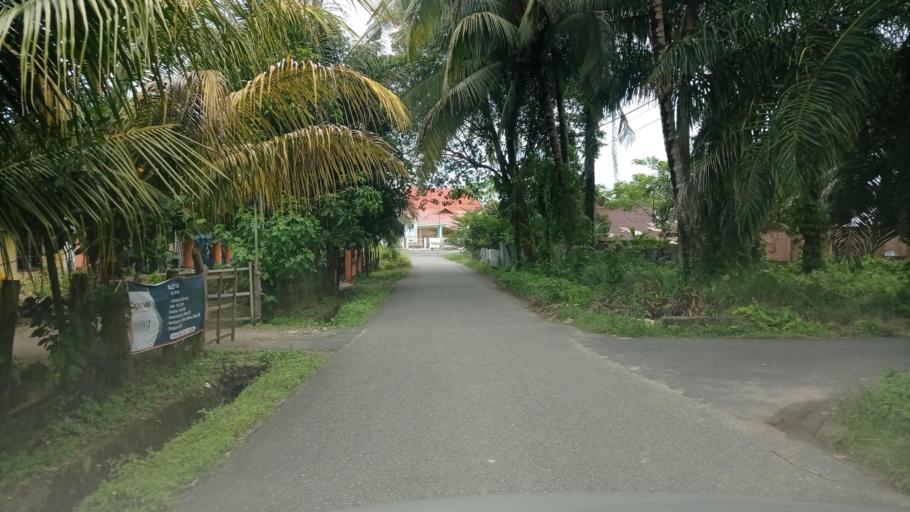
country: ID
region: Bengkulu
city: Ipuh
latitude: -2.5635
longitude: 101.1068
